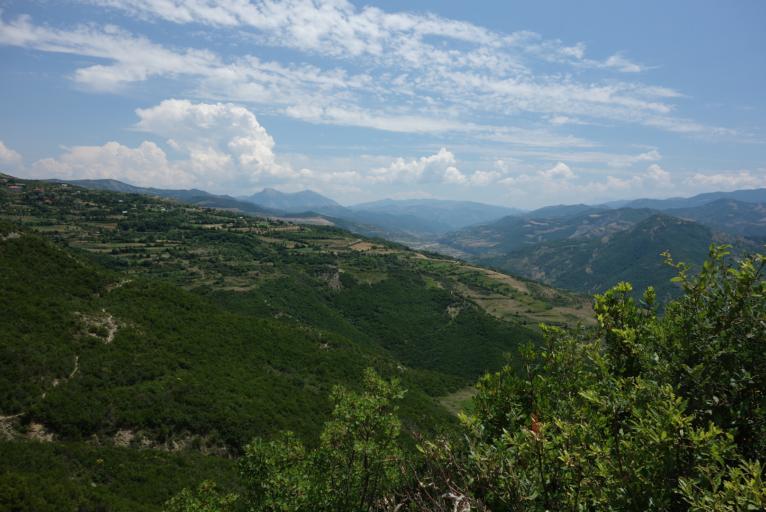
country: AL
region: Berat
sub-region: Rrethi i Skraparit
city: Corovode
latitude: 40.5298
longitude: 20.1918
